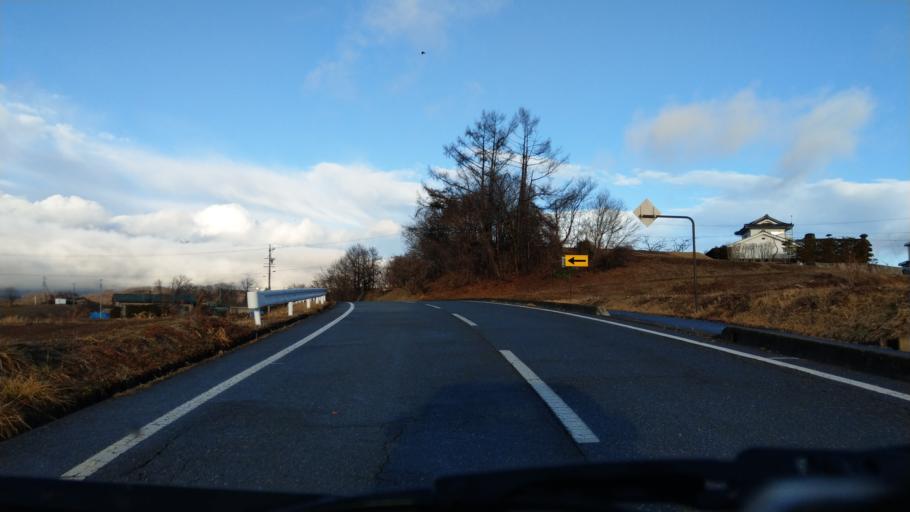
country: JP
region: Nagano
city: Komoro
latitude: 36.3042
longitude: 138.3784
